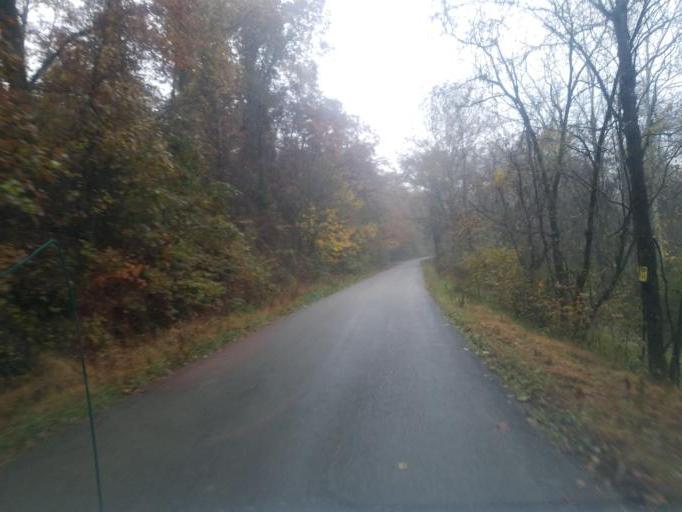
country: US
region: Ohio
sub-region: Athens County
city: Glouster
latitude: 39.5001
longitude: -81.9511
